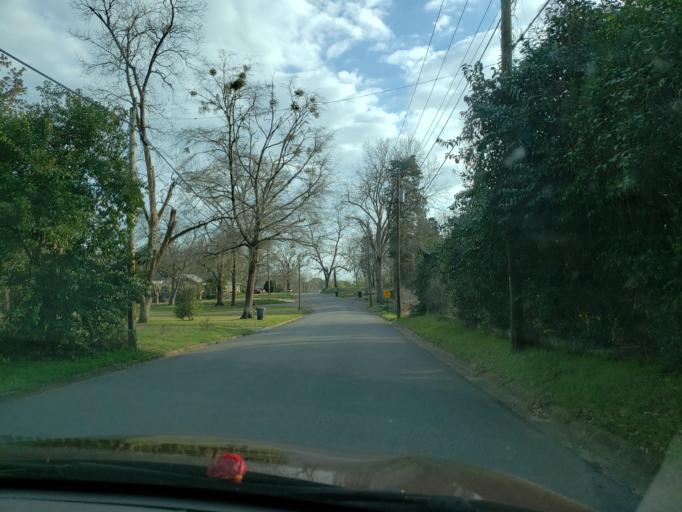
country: US
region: Alabama
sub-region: Hale County
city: Greensboro
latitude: 32.7027
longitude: -87.5922
